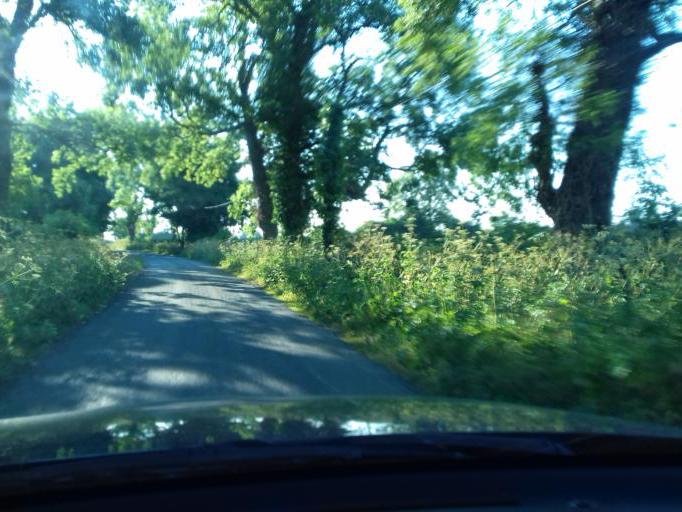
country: IE
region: Leinster
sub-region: An Mhi
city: Ashbourne
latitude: 53.4768
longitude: -6.3239
